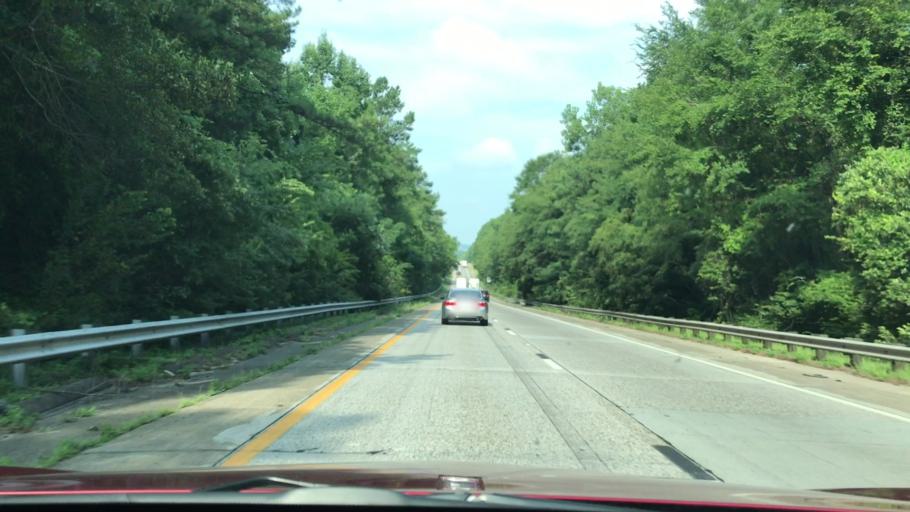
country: US
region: South Carolina
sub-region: Aiken County
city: Belvedere
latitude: 33.5452
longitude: -81.9720
